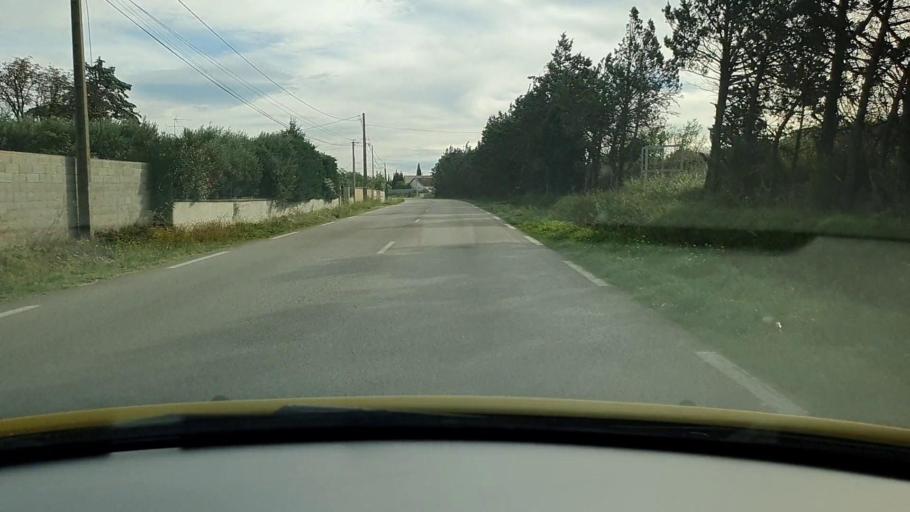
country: FR
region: Languedoc-Roussillon
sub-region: Departement du Gard
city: Beaucaire
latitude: 43.7952
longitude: 4.5999
